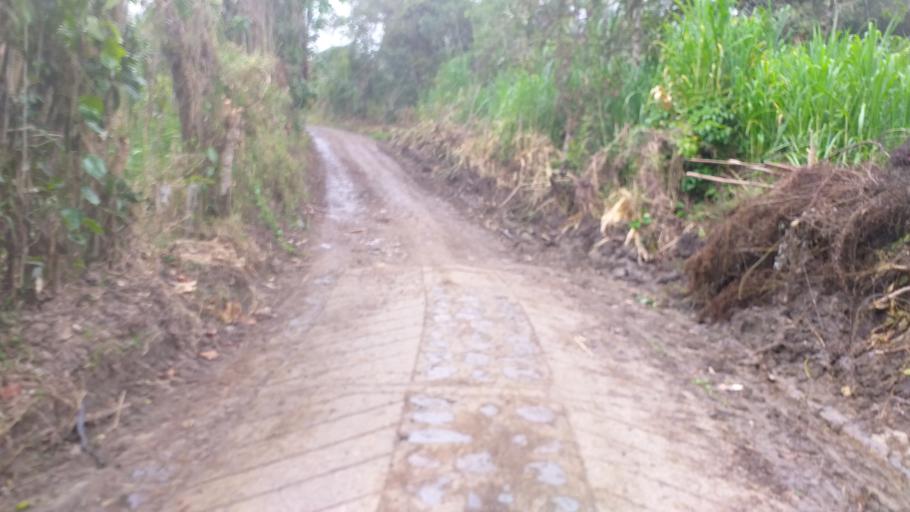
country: CO
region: Cundinamarca
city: Tenza
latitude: 5.0870
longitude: -73.4558
